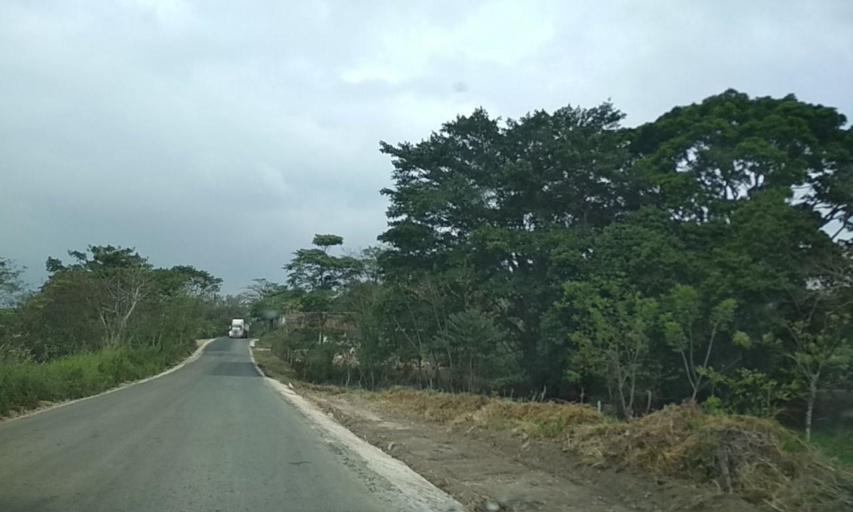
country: MX
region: Tabasco
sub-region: Huimanguillo
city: Francisco Rueda
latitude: 17.7254
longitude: -94.1007
